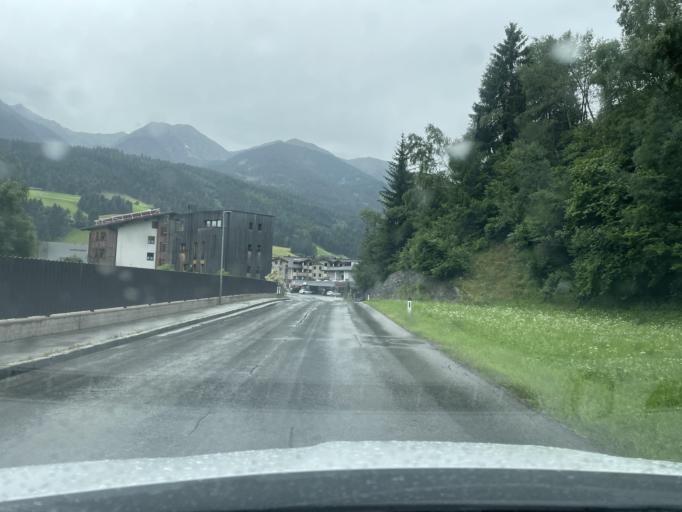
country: AT
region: Tyrol
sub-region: Politischer Bezirk Lienz
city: Heinfels
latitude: 46.7510
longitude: 12.4363
